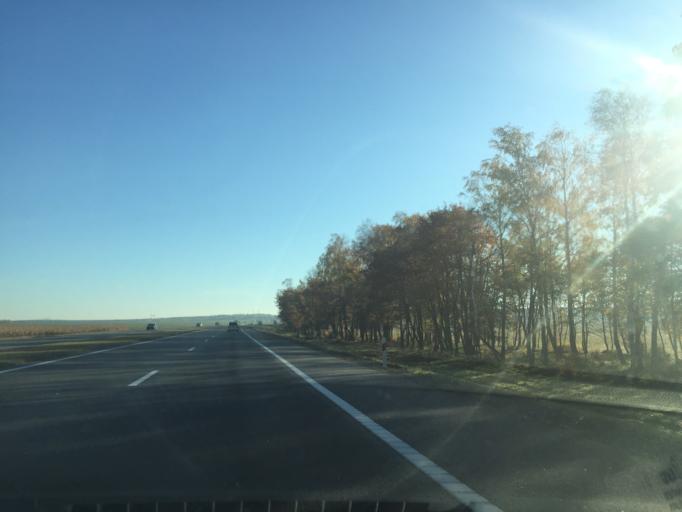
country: BY
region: Minsk
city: Smilavichy
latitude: 53.7633
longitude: 28.0830
